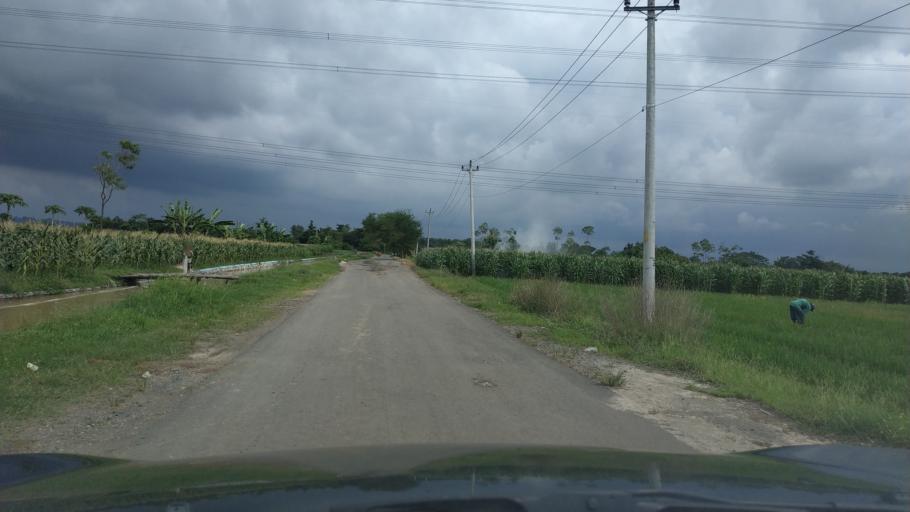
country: ID
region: Central Java
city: Pemalang
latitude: -6.9372
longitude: 109.3369
